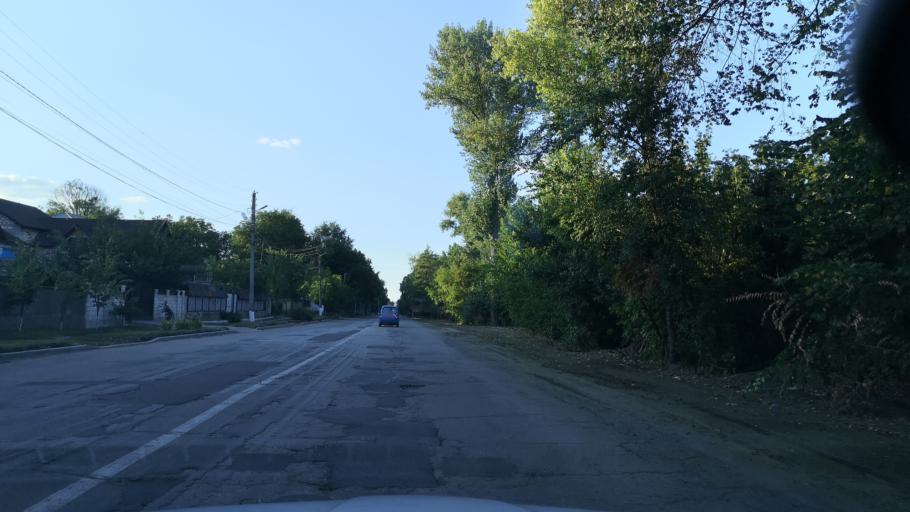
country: MD
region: Orhei
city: Orhei
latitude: 47.3920
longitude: 28.8226
